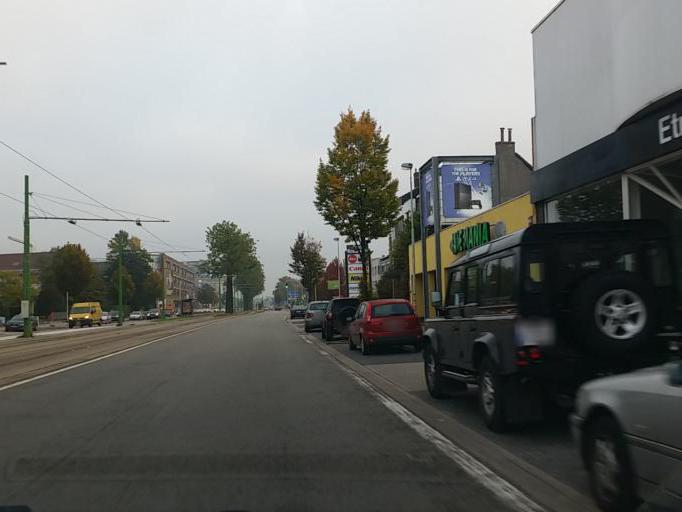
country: BE
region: Flanders
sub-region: Provincie Antwerpen
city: Schoten
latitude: 51.2500
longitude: 4.4552
